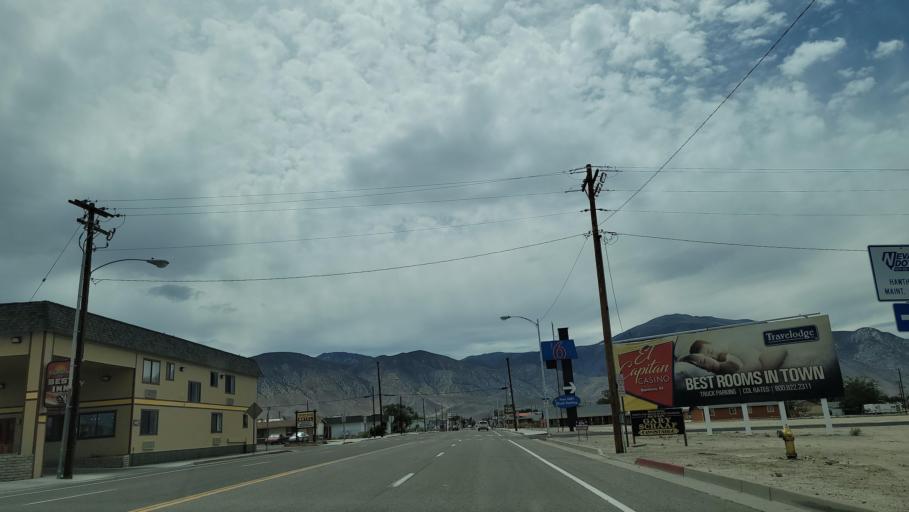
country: US
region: Nevada
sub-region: Mineral County
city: Hawthorne
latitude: 38.5246
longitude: -118.6153
